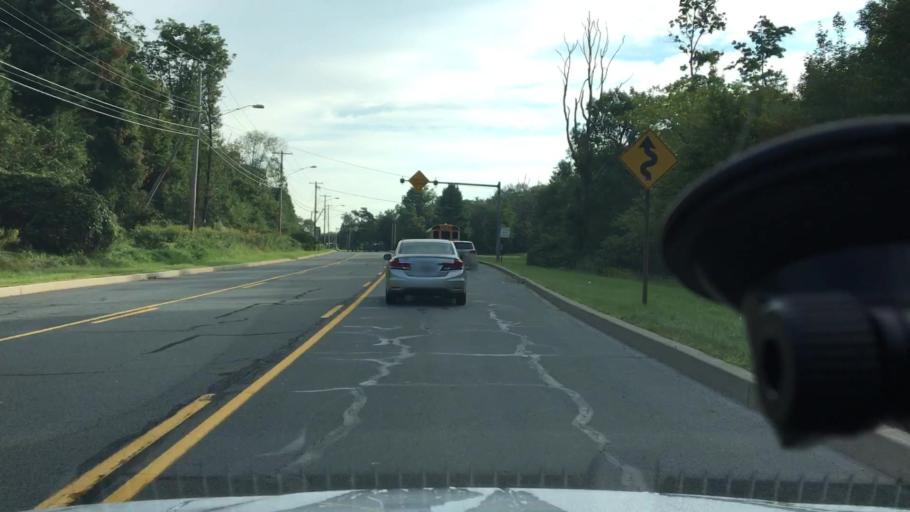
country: US
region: Pennsylvania
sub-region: Monroe County
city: Mount Pocono
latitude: 41.1042
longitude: -75.3299
